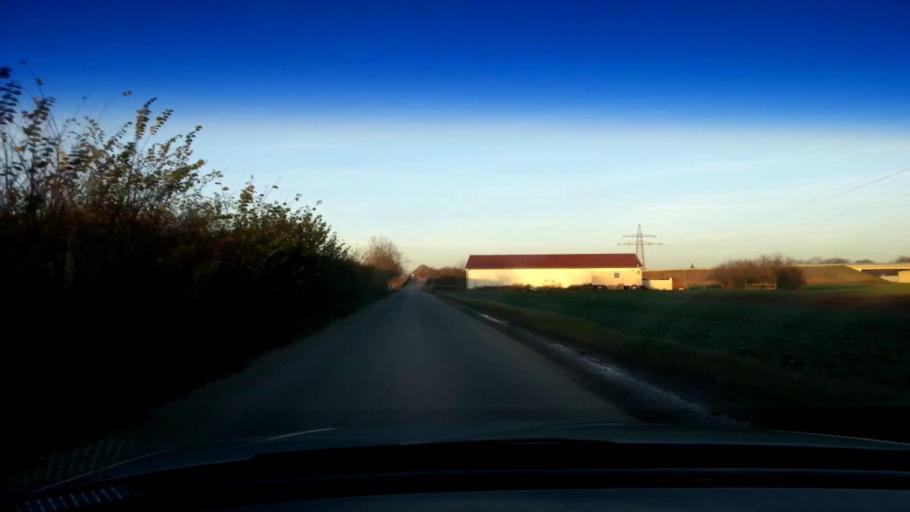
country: DE
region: Bavaria
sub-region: Upper Franconia
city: Ebensfeld
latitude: 50.0586
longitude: 10.9484
